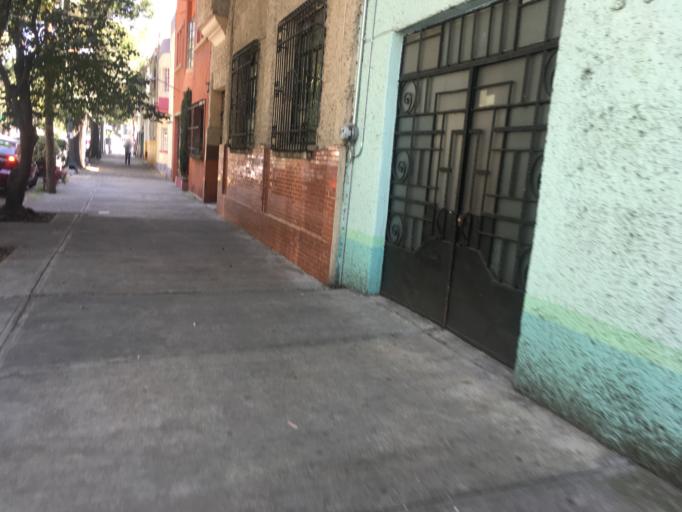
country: MX
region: Mexico City
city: Benito Juarez
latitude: 19.4075
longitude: -99.1578
